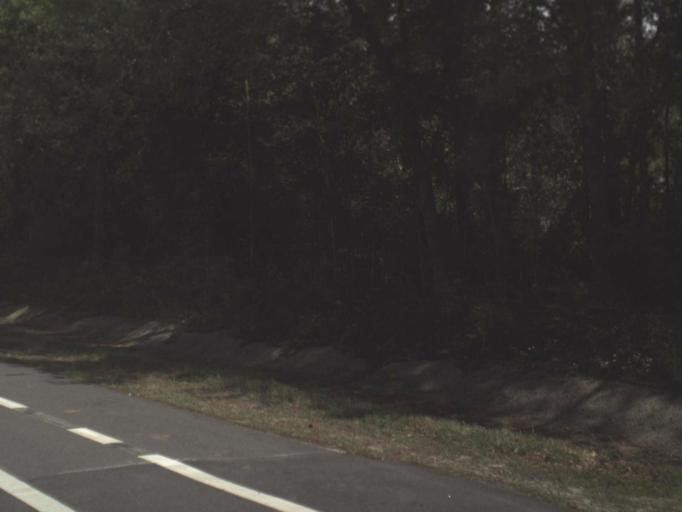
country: US
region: Florida
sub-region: Santa Rosa County
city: East Milton
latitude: 30.6360
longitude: -86.9677
